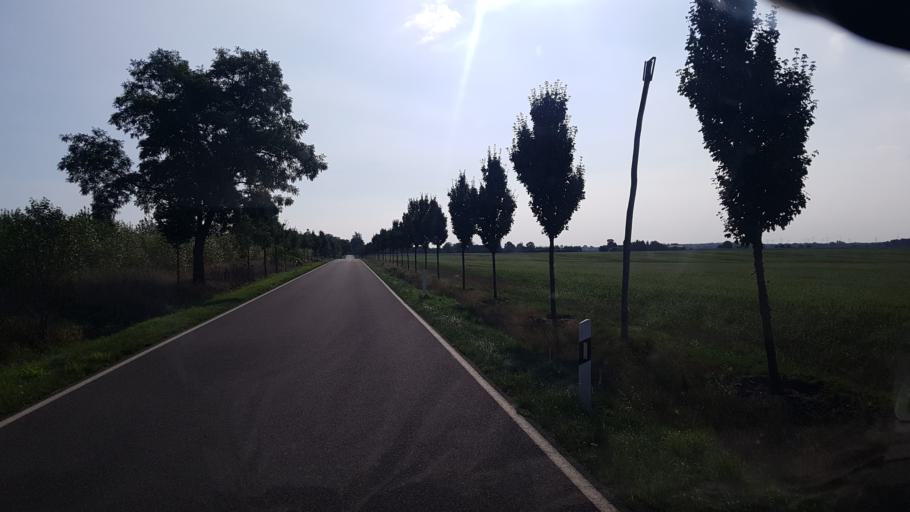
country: DE
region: Brandenburg
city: Luebben
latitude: 51.8825
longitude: 13.8324
